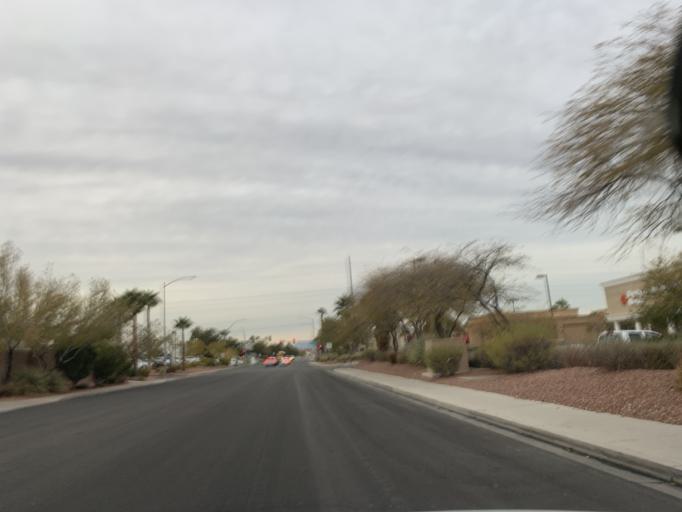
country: US
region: Nevada
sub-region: Clark County
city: Summerlin South
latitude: 36.1576
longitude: -115.2846
